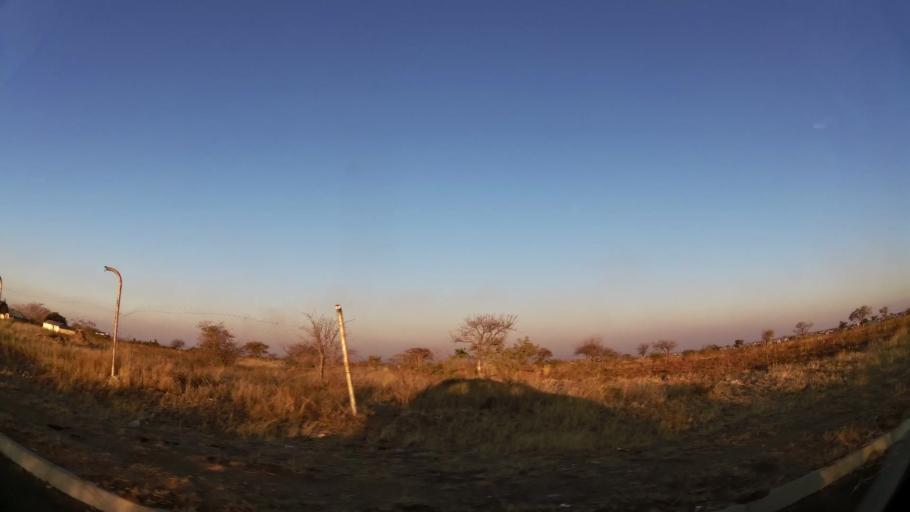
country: ZA
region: Limpopo
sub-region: Capricorn District Municipality
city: Polokwane
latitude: -23.8602
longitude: 29.3747
